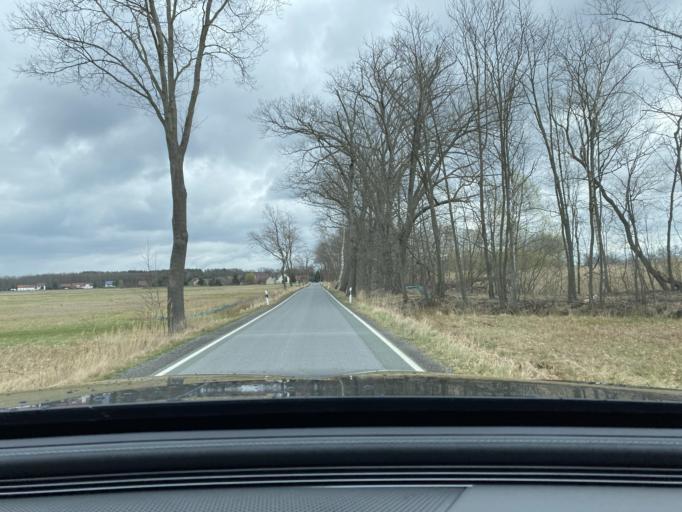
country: DE
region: Saxony
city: Uhyst
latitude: 51.3303
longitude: 14.4811
